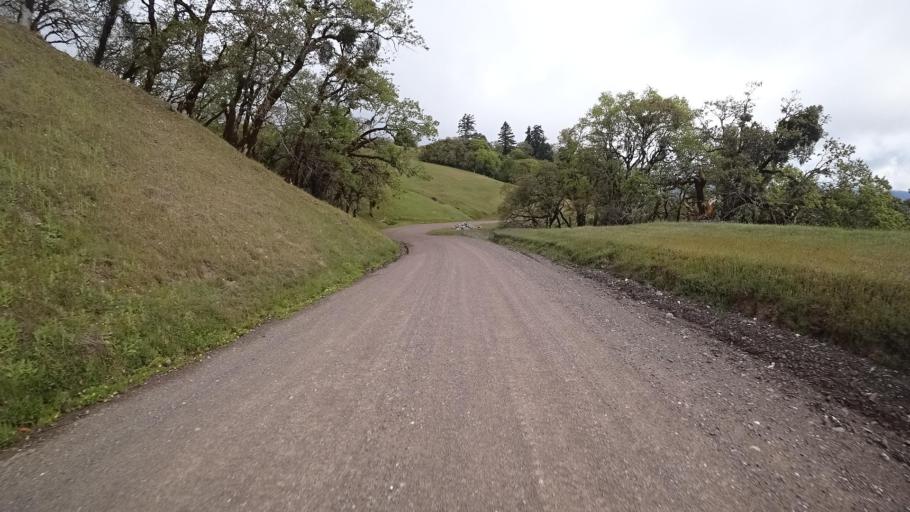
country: US
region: California
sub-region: Humboldt County
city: Redway
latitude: 40.1972
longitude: -123.7022
